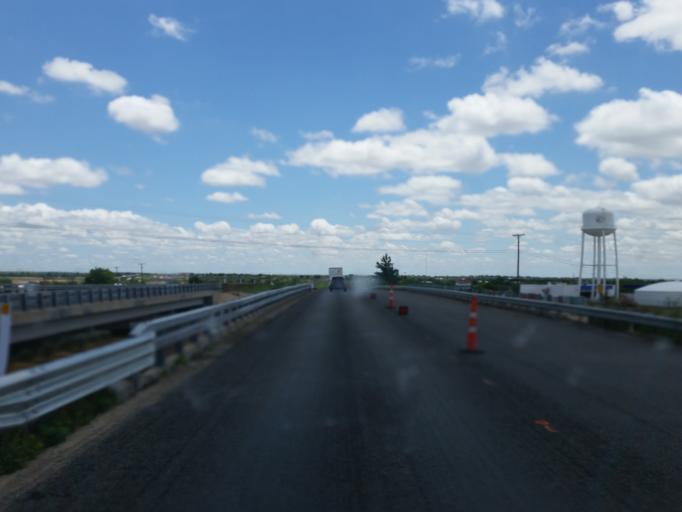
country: US
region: Texas
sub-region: Scurry County
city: Snyder
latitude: 32.7394
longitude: -100.9188
